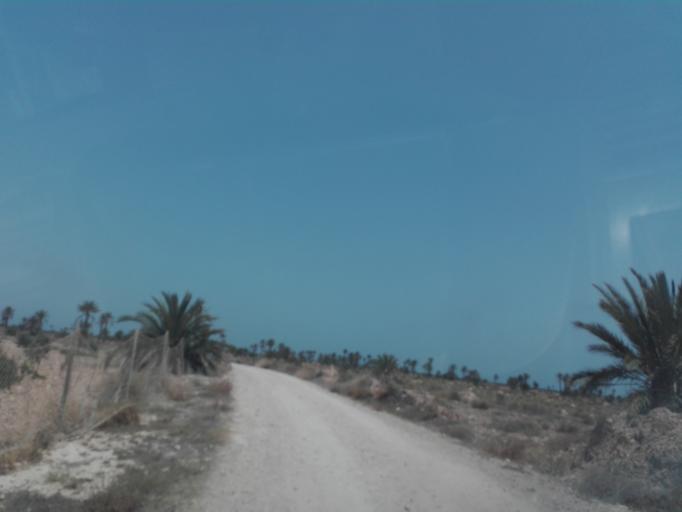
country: TN
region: Safaqis
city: Al Qarmadah
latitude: 34.6614
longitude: 11.0988
